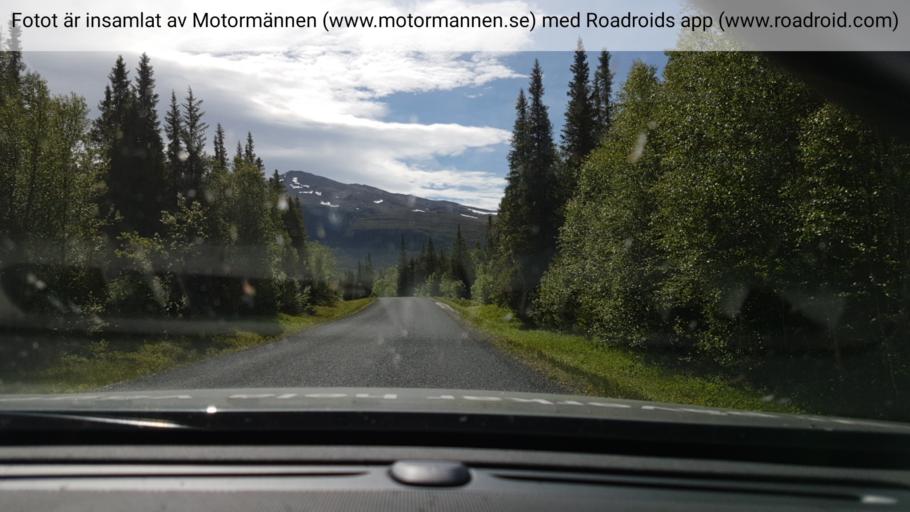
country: SE
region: Vaesterbotten
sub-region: Vilhelmina Kommun
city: Sjoberg
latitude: 65.2526
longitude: 15.4184
